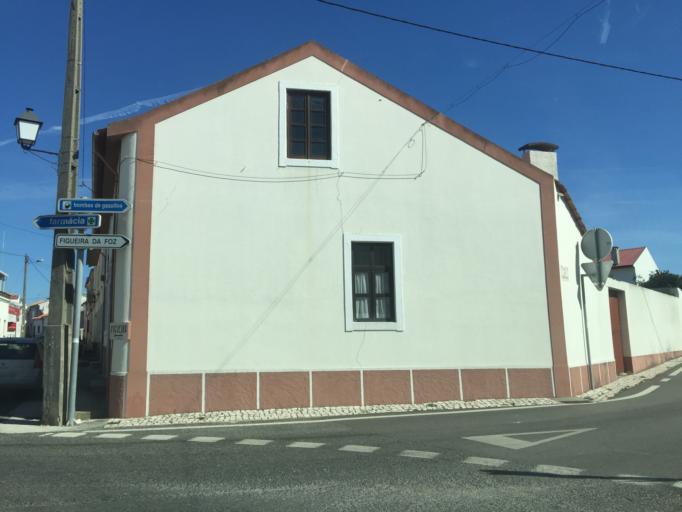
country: PT
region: Coimbra
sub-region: Figueira da Foz
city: Tavarede
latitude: 40.2130
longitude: -8.8496
